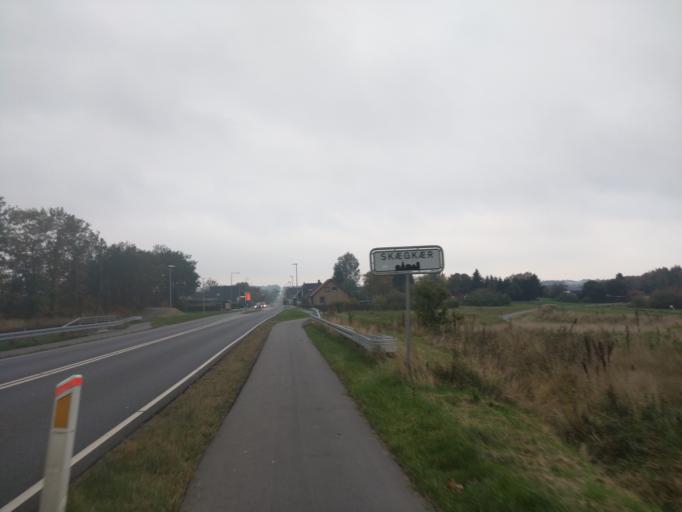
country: DK
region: Central Jutland
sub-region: Silkeborg Kommune
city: Silkeborg
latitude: 56.2106
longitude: 9.5051
